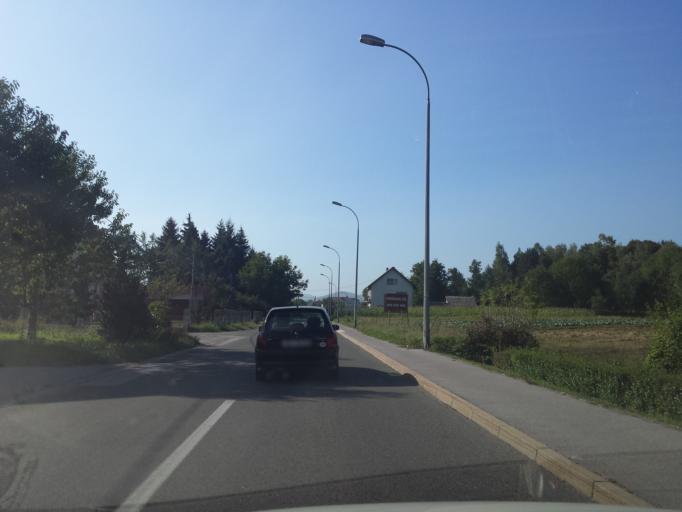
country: HR
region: Karlovacka
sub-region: Grad Ogulin
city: Ogulin
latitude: 45.2475
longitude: 15.2447
